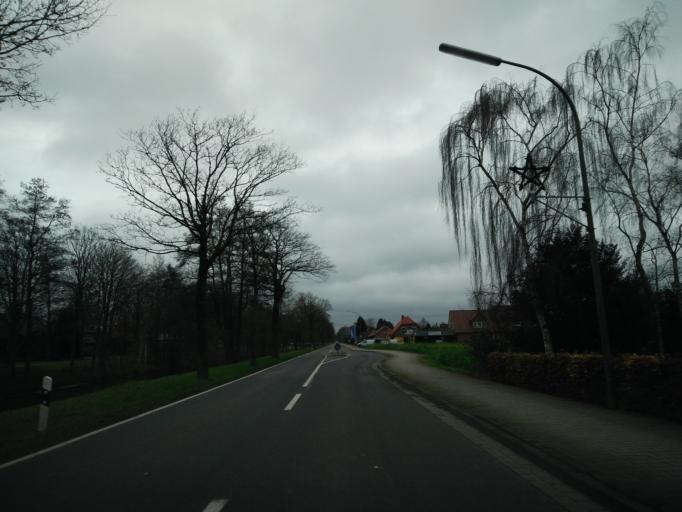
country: NL
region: Drenthe
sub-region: Gemeente Emmen
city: Emmer-Compascuum
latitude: 52.7826
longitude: 7.1077
